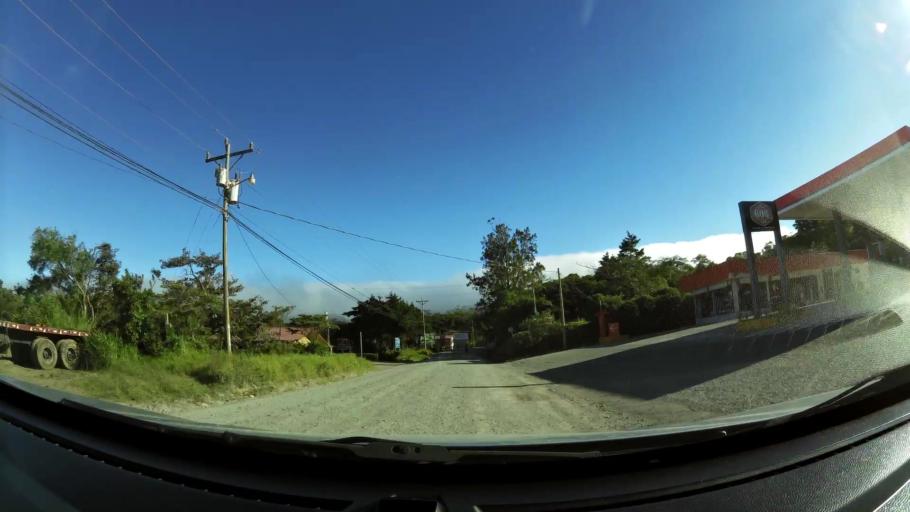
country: CR
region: Guanacaste
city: Juntas
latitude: 10.3050
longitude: -84.8326
